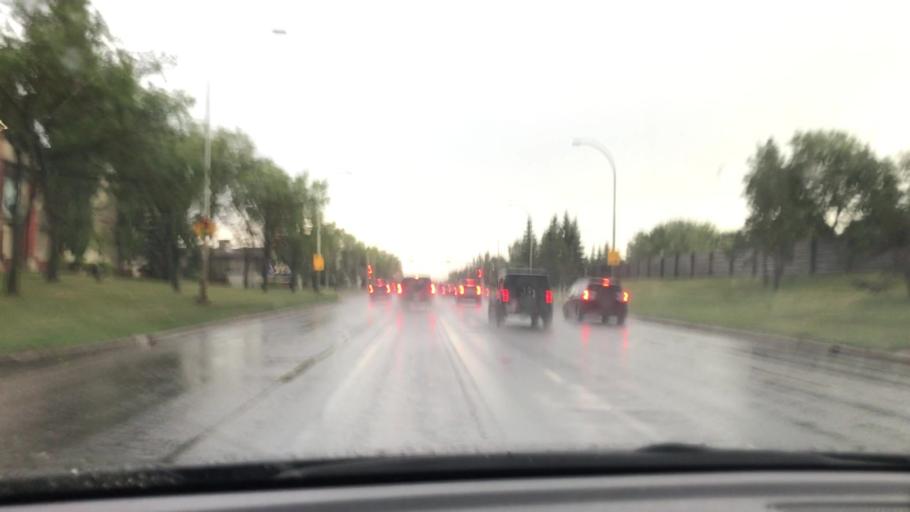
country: CA
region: Alberta
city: Edmonton
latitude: 53.4736
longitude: -113.4957
